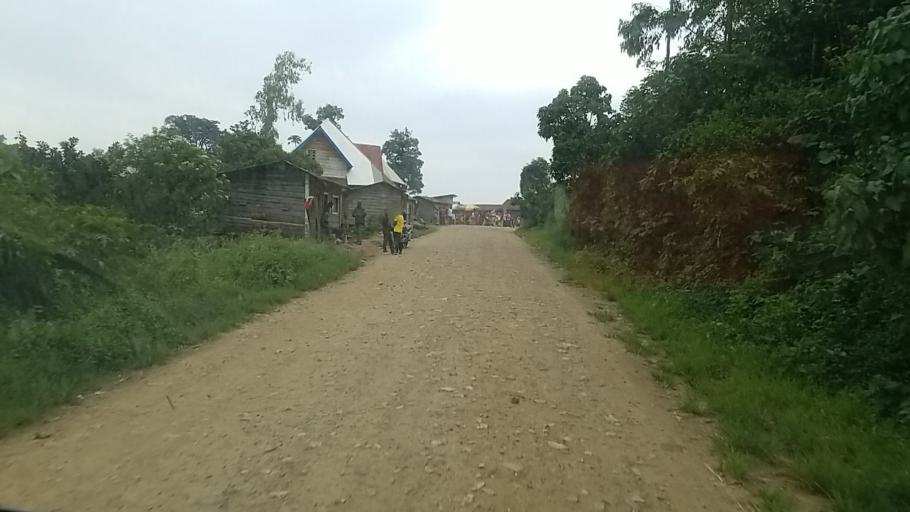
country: CD
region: Nord Kivu
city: Sake
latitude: -1.9580
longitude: 28.9220
